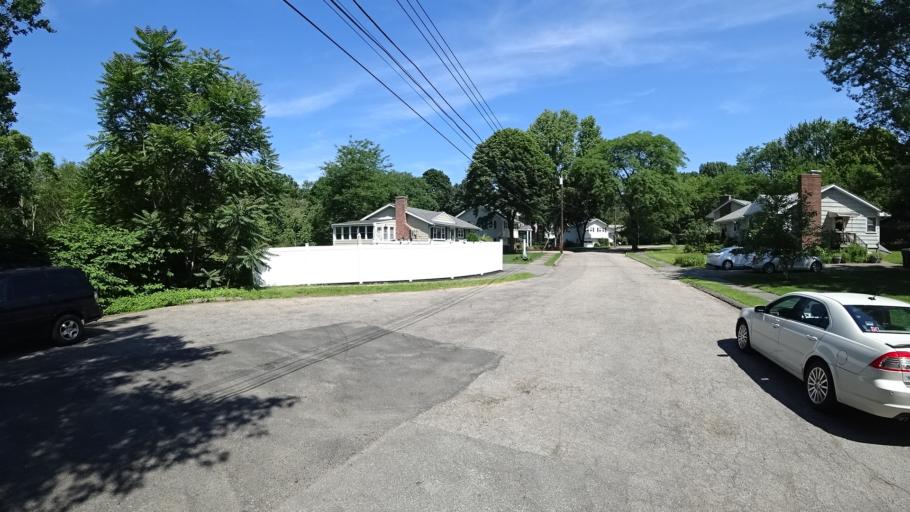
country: US
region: Massachusetts
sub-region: Norfolk County
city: Dedham
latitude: 42.2400
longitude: -71.1668
